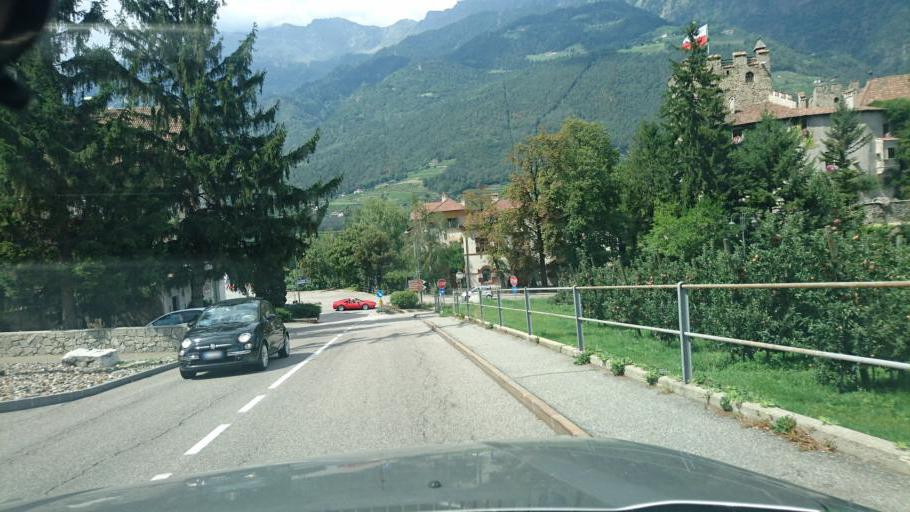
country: IT
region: Trentino-Alto Adige
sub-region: Bolzano
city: Lagundo
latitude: 46.6775
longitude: 11.1196
